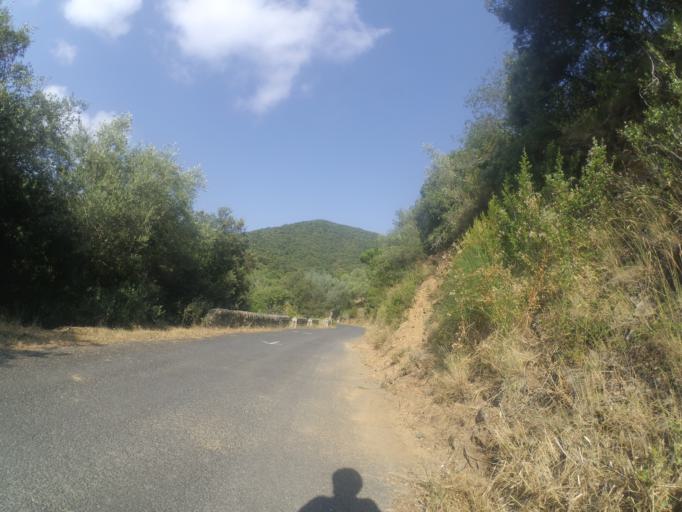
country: FR
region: Languedoc-Roussillon
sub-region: Departement des Pyrenees-Orientales
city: Ille-sur-Tet
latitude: 42.6451
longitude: 2.6267
